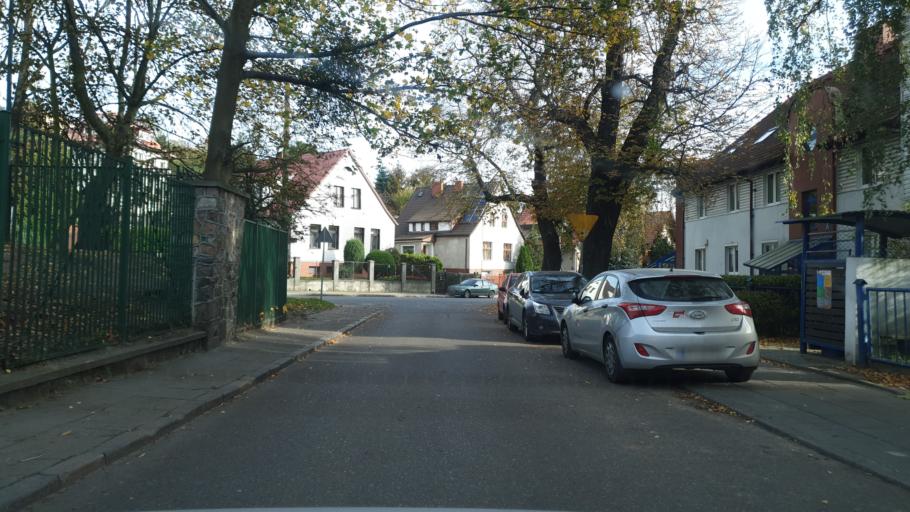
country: PL
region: Pomeranian Voivodeship
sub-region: Gdansk
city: Gdansk
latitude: 54.3516
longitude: 18.6283
